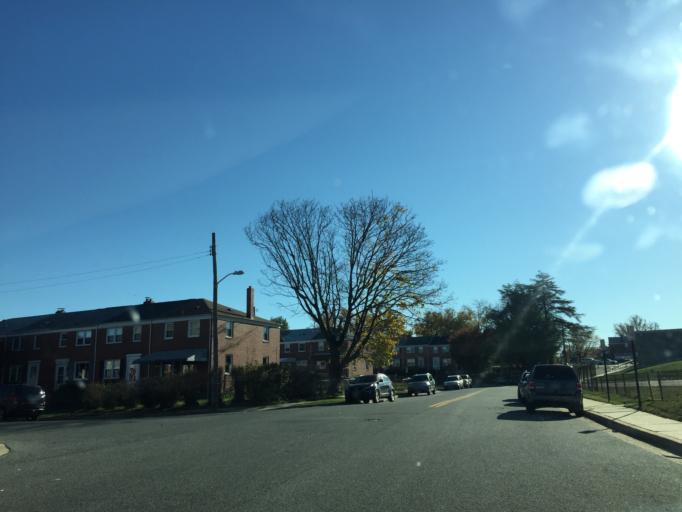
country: US
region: Maryland
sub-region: Baltimore County
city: Parkville
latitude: 39.3923
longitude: -76.5620
